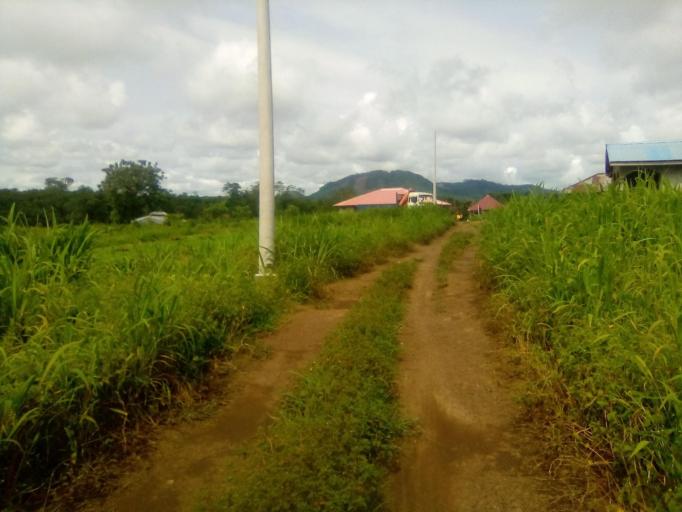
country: SL
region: Southern Province
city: Moyamba
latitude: 8.1451
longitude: -12.4311
